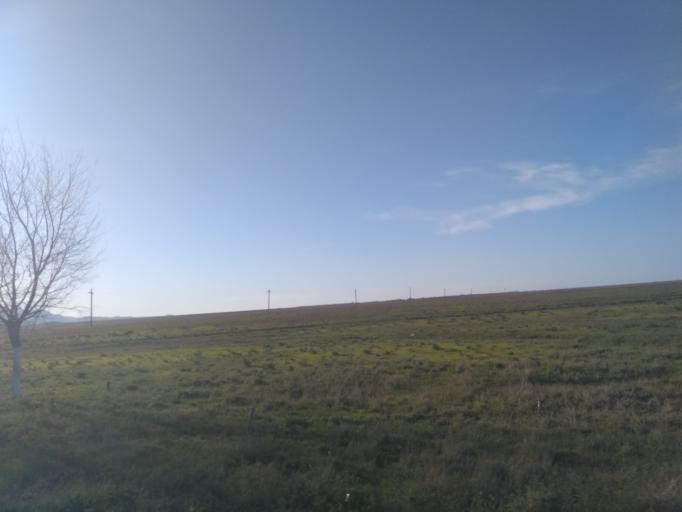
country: KZ
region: Ongtustik Qazaqstan
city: Ashchysay
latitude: 43.6945
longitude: 68.9968
